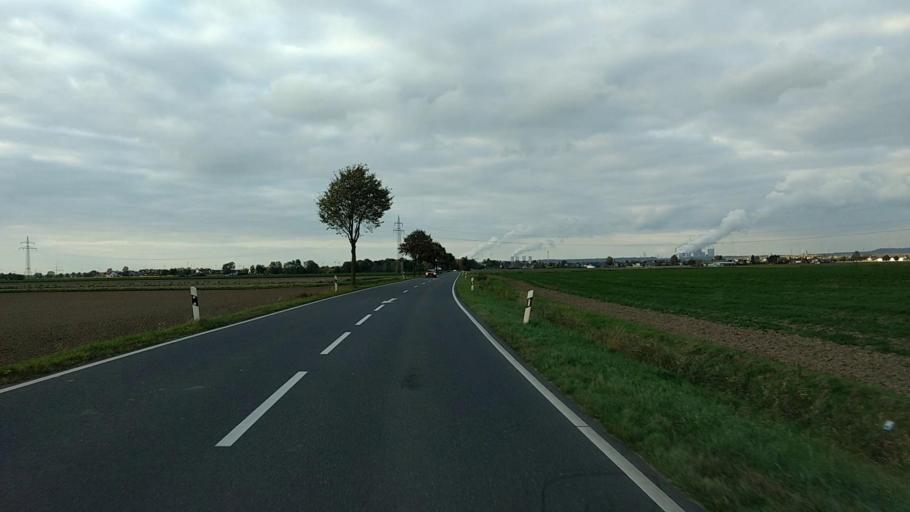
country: DE
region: North Rhine-Westphalia
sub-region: Regierungsbezirk Koln
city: Bergheim
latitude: 50.9001
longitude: 6.6411
